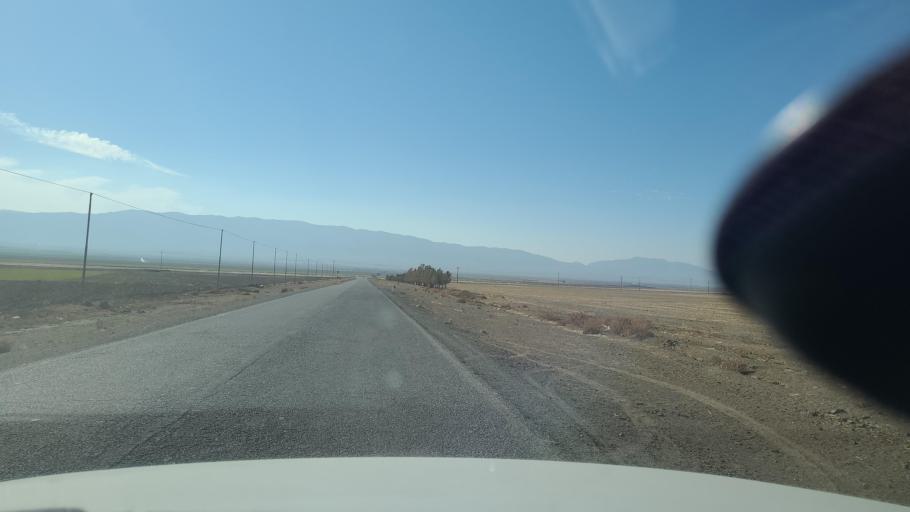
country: IR
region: Razavi Khorasan
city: Dowlatabad
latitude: 35.6034
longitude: 59.4626
